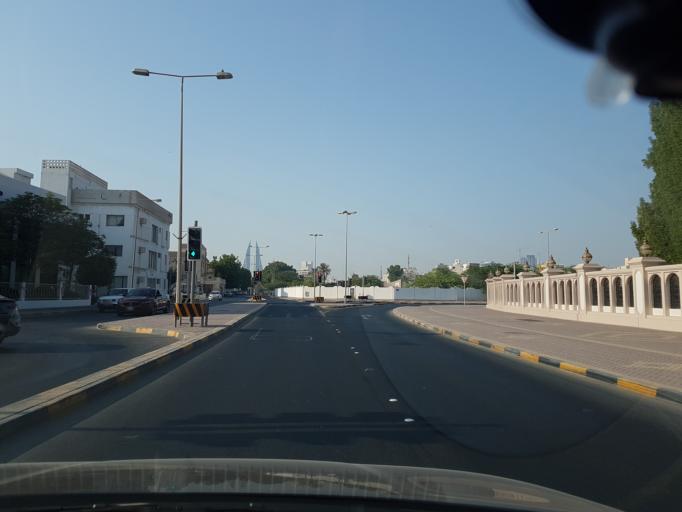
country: BH
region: Manama
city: Manama
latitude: 26.2194
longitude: 50.5901
